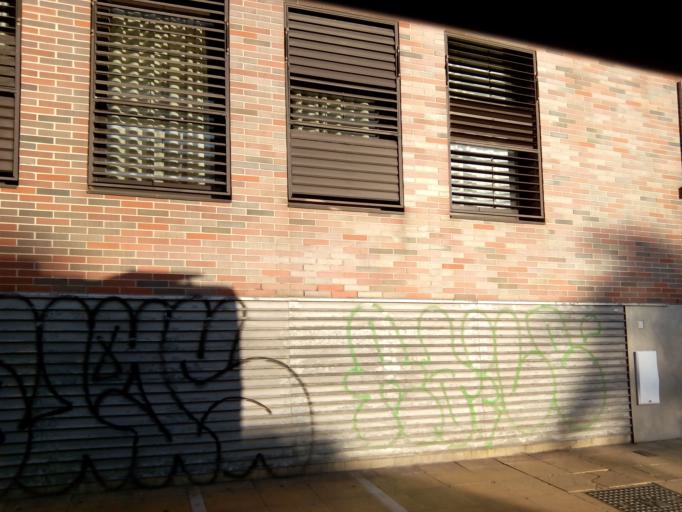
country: ES
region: Andalusia
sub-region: Provincia de Sevilla
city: Sevilla
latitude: 37.3985
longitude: -6.0001
